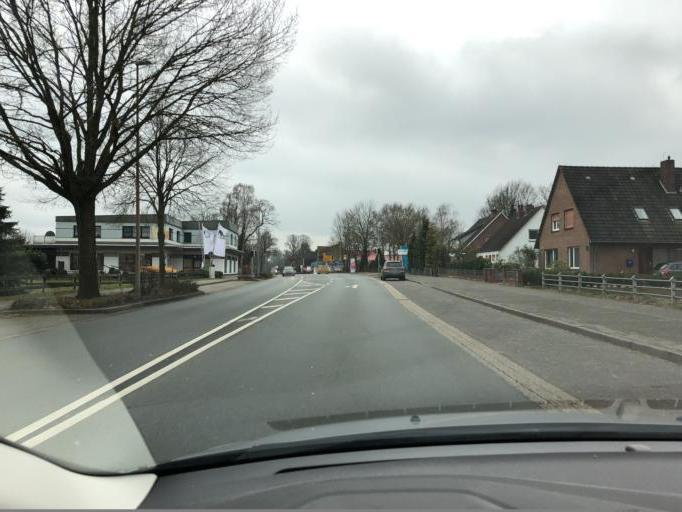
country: DE
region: Lower Saxony
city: Ganderkesee
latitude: 53.0929
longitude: 8.5299
